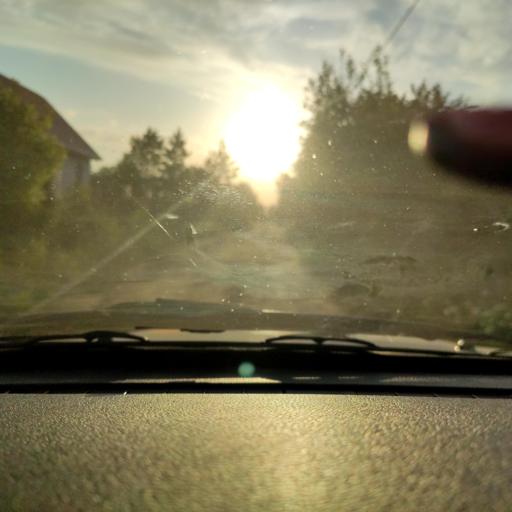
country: RU
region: Voronezj
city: Podgornoye
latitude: 51.8345
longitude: 39.1921
